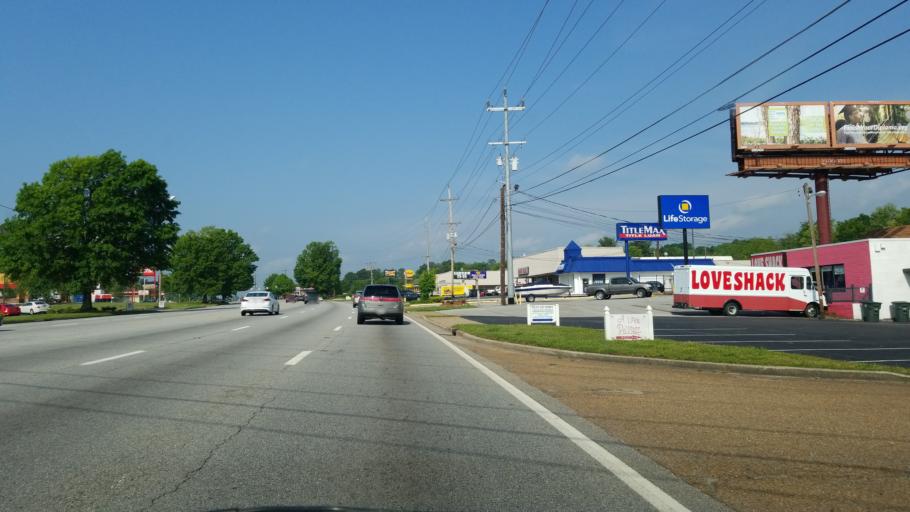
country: US
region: Tennessee
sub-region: Hamilton County
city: East Chattanooga
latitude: 35.0847
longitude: -85.1996
